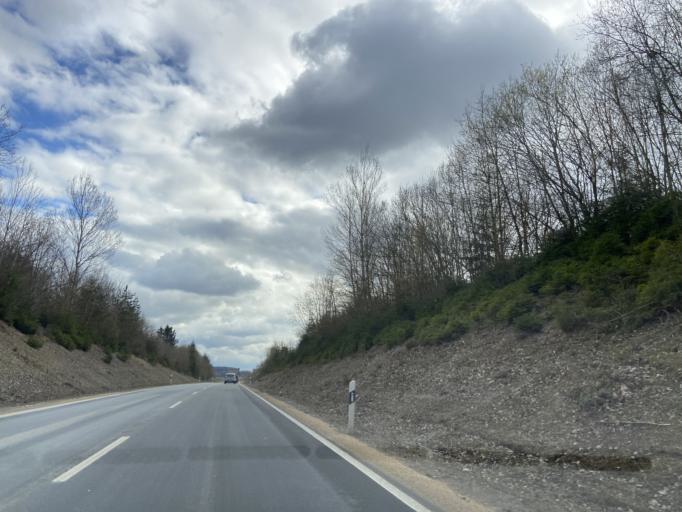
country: DE
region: Baden-Wuerttemberg
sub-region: Tuebingen Region
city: Ostrach
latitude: 47.9545
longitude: 9.3968
